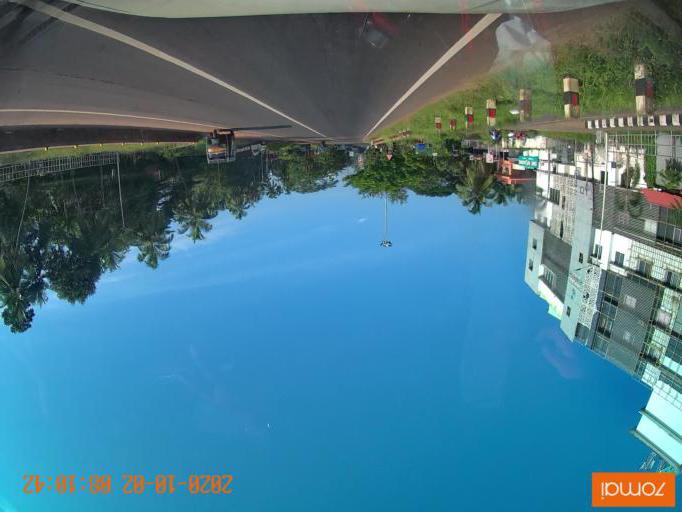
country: IN
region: Kerala
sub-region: Kozhikode
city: Kozhikode
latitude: 11.2691
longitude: 75.8099
